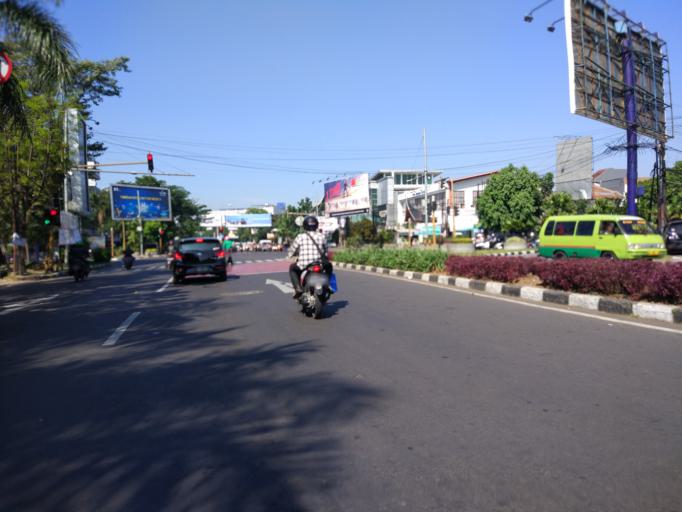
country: ID
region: West Java
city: Bandung
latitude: -6.9320
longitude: 107.6259
